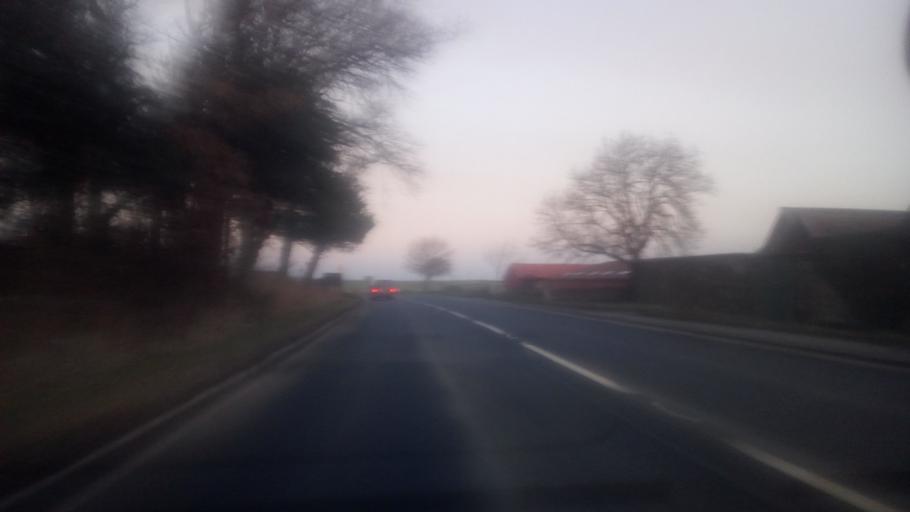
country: GB
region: Scotland
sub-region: East Lothian
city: Pencaitland
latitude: 55.8381
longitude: -2.9015
